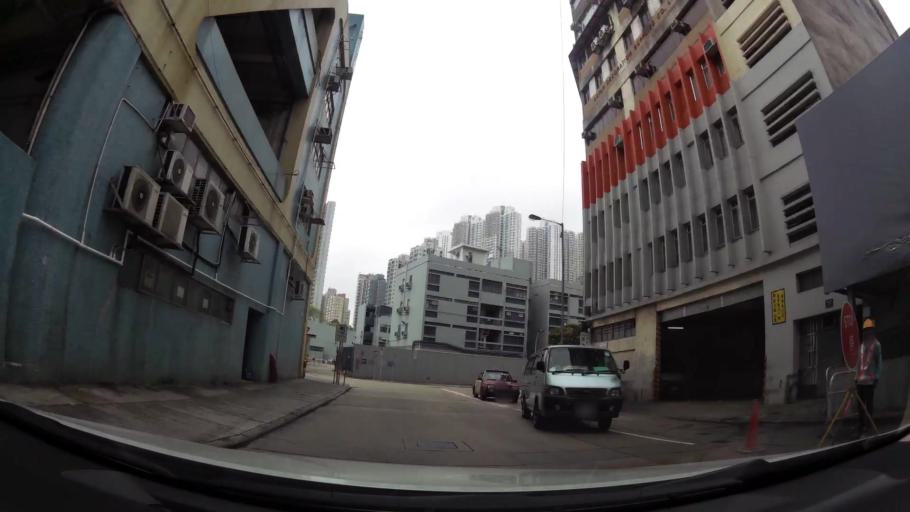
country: HK
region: Wanchai
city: Wan Chai
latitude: 22.2480
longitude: 114.1621
